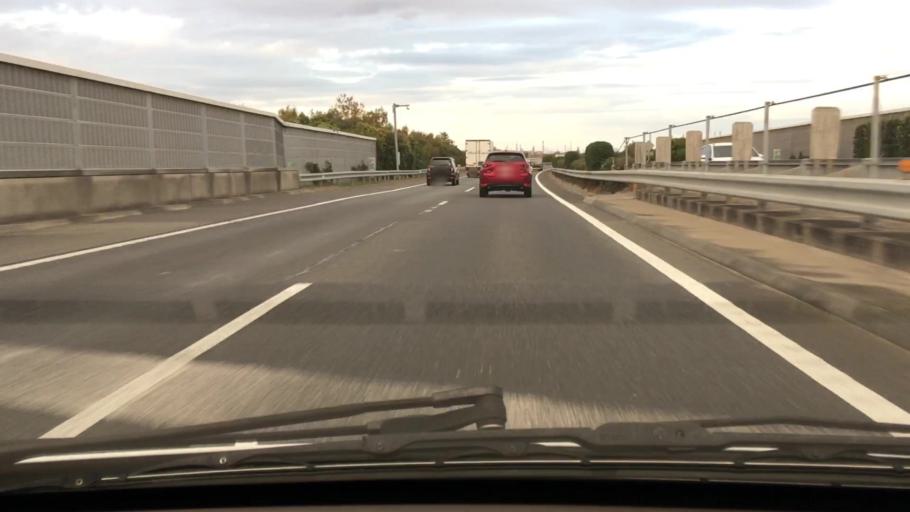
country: JP
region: Chiba
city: Ichihara
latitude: 35.4751
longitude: 140.0820
